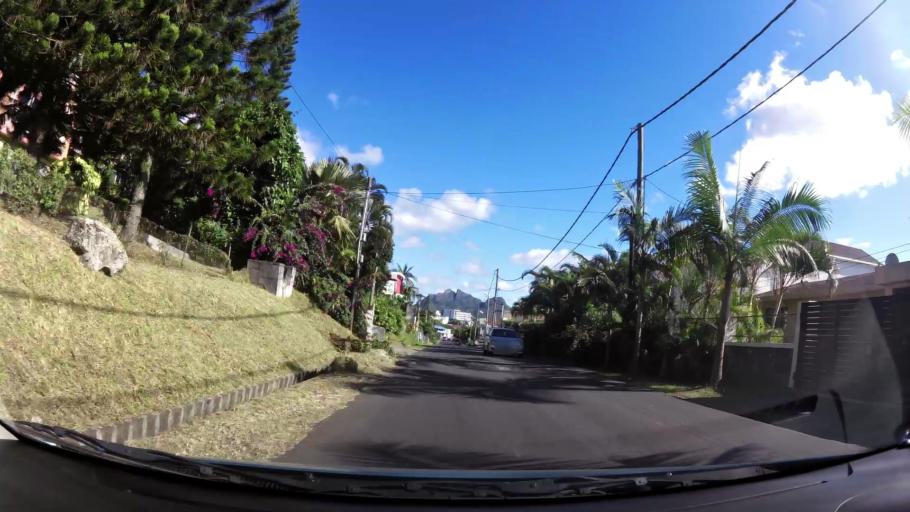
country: MU
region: Plaines Wilhems
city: Quatre Bornes
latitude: -20.2743
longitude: 57.4808
